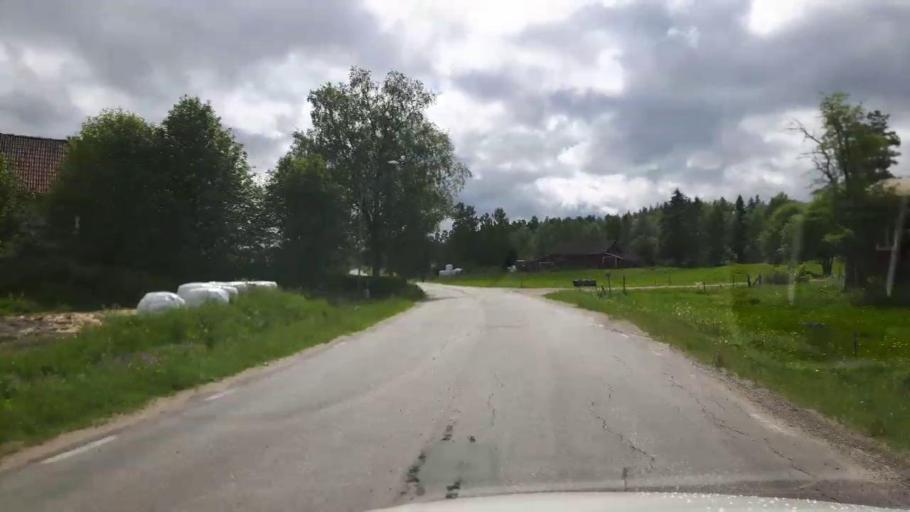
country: SE
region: Gaevleborg
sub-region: Ovanakers Kommun
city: Edsbyn
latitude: 61.3491
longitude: 15.9202
